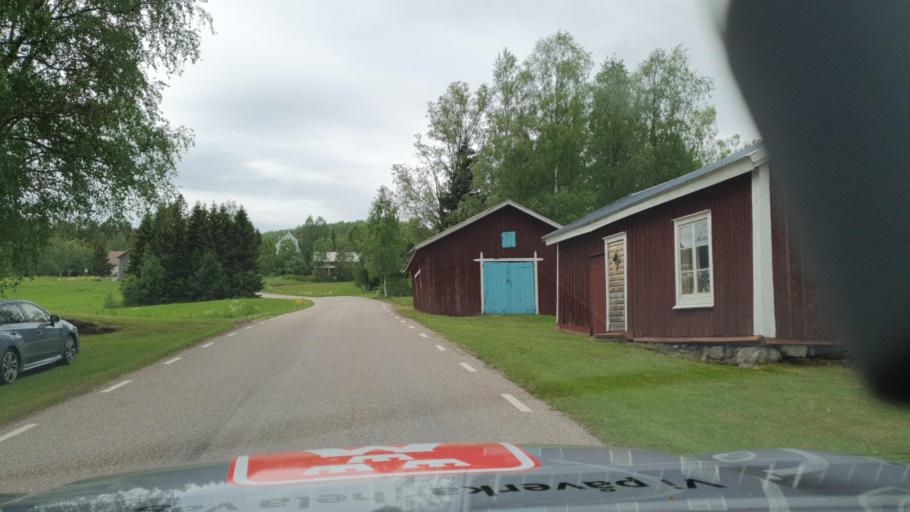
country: SE
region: Vaesternorrland
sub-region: Kramfors Kommun
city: Nordingra
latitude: 62.8847
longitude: 18.3953
